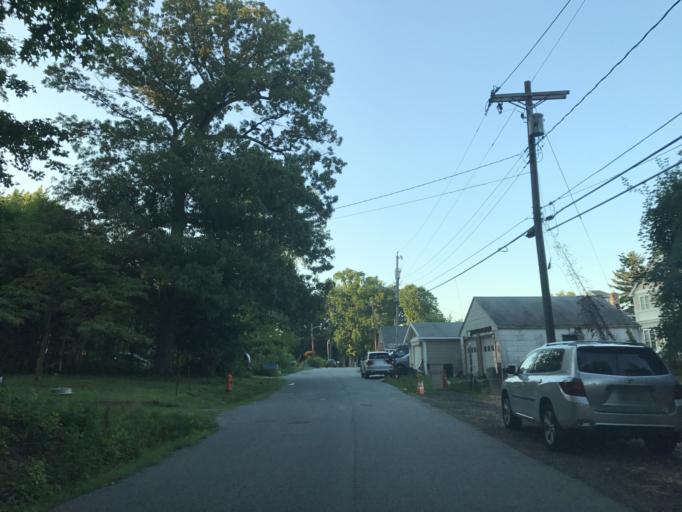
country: US
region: Maryland
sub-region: Baltimore County
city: Edgemere
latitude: 39.2655
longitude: -76.3976
